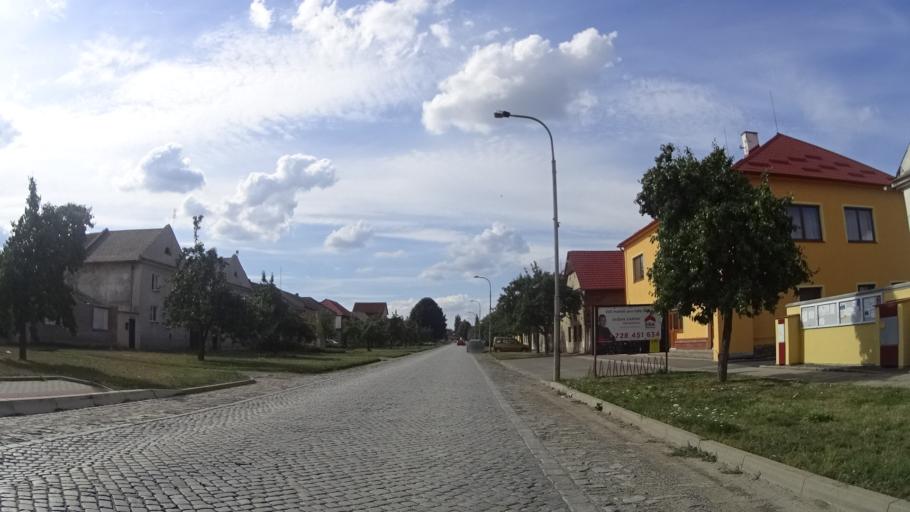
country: CZ
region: Olomoucky
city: Moravicany
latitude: 49.7560
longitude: 16.9621
